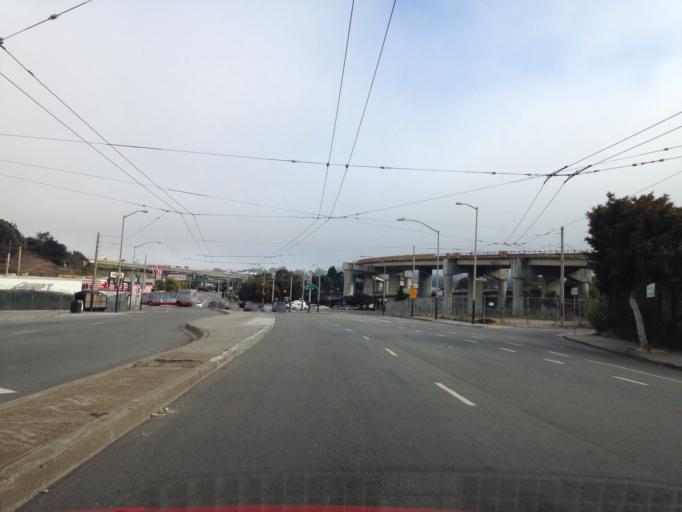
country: US
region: California
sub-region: San Francisco County
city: San Francisco
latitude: 37.7392
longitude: -122.4071
